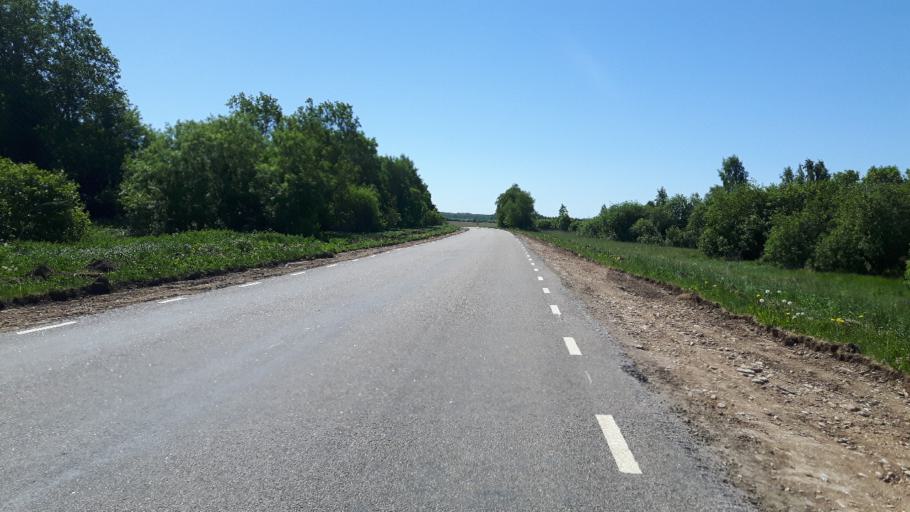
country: EE
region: Ida-Virumaa
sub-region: Narva-Joesuu linn
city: Narva-Joesuu
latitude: 59.3901
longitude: 27.9214
